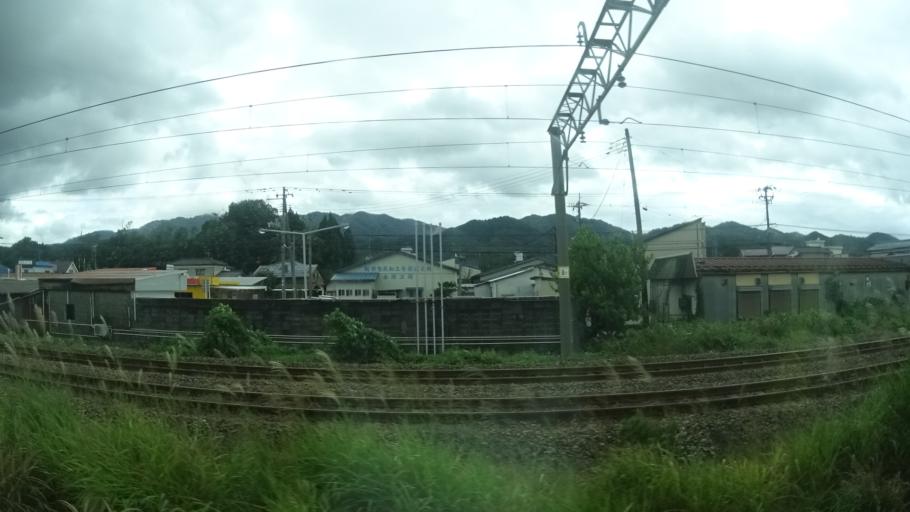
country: JP
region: Niigata
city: Shibata
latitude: 38.0187
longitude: 139.3788
